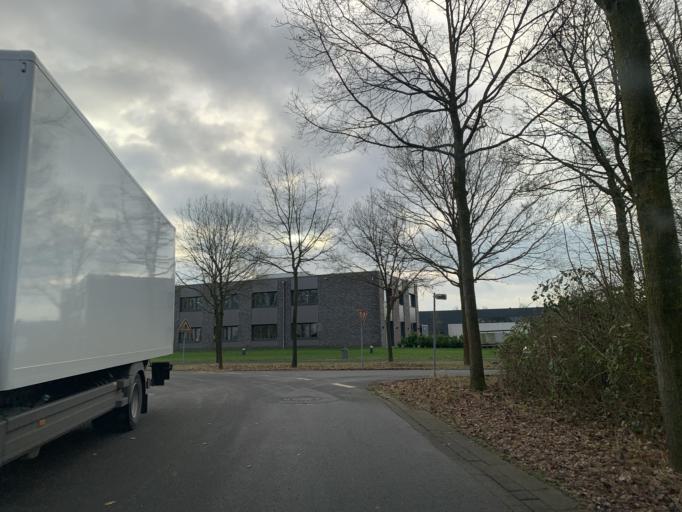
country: DE
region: North Rhine-Westphalia
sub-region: Regierungsbezirk Munster
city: Senden
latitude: 51.9075
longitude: 7.4765
